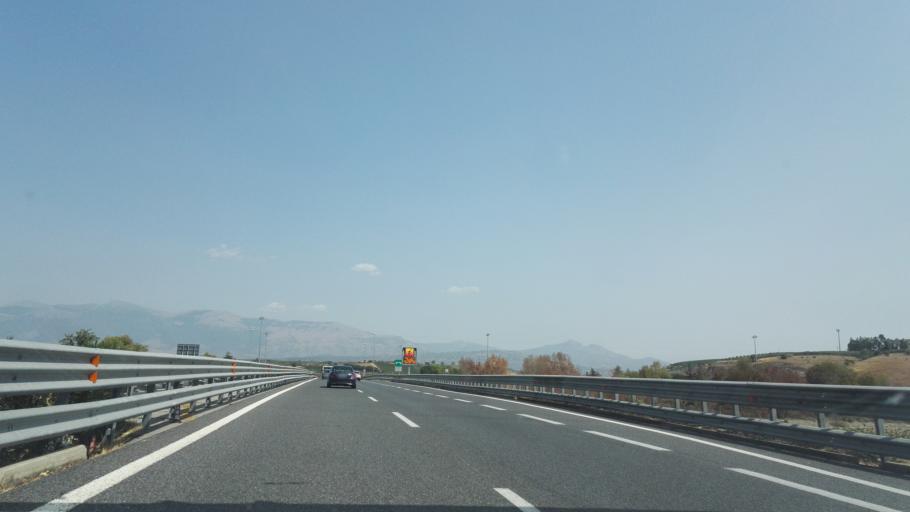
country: IT
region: Calabria
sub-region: Provincia di Cosenza
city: Firmo
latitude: 39.6761
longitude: 16.2178
